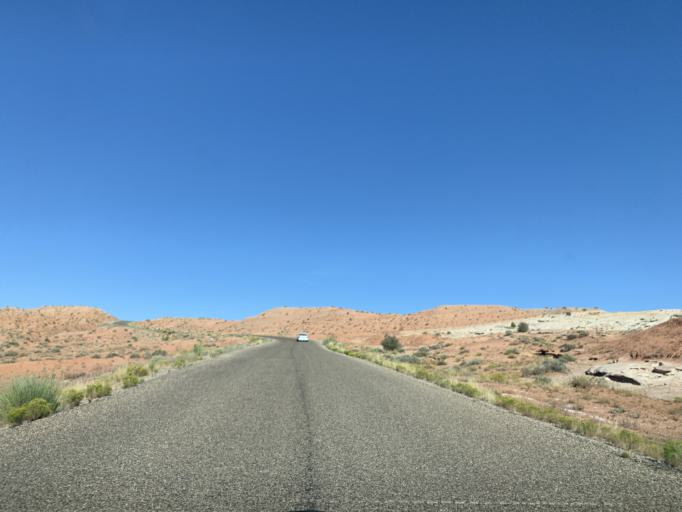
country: US
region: Utah
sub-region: Emery County
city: Ferron
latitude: 38.5813
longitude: -110.7793
